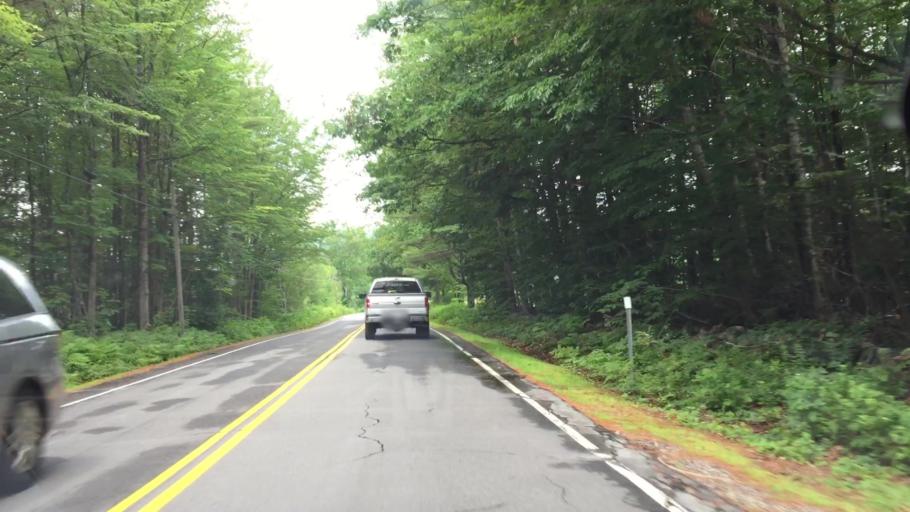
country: US
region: New Hampshire
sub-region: Carroll County
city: Sandwich
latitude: 43.8047
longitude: -71.4551
